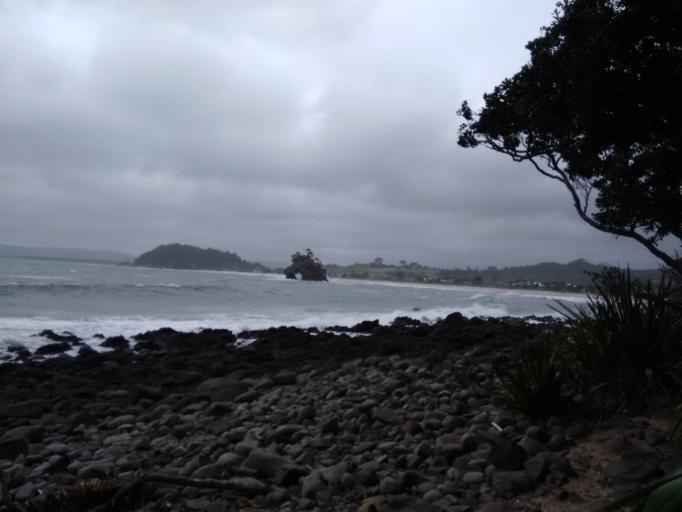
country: NZ
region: Waikato
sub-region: Thames-Coromandel District
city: Coromandel
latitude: -36.7033
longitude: 175.6107
